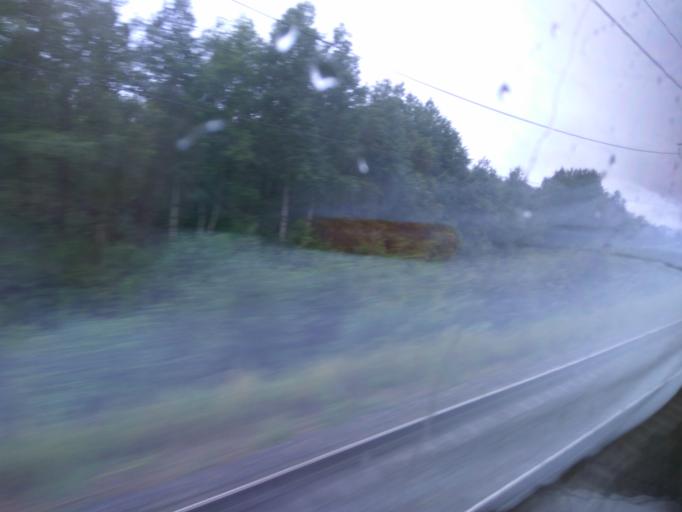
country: RU
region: Moskovskaya
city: Kashira
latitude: 54.8543
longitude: 38.2162
